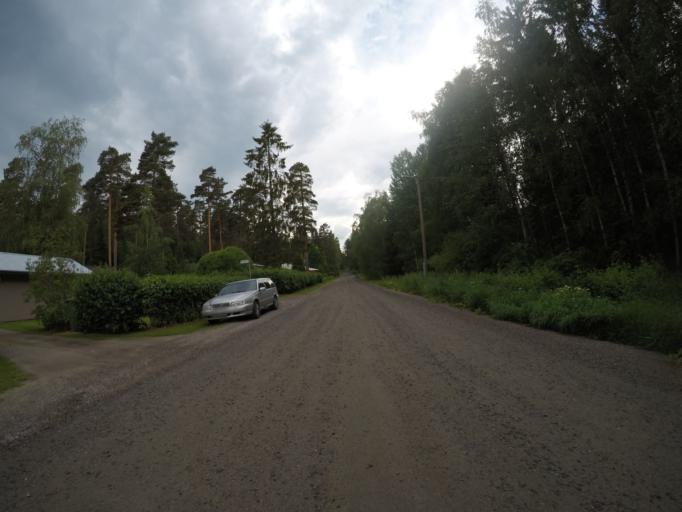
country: FI
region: Haeme
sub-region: Haemeenlinna
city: Haemeenlinna
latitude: 61.0121
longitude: 24.4904
